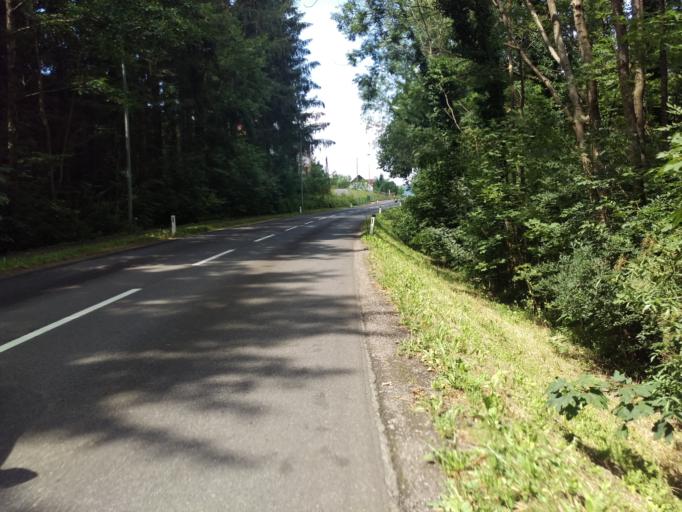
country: AT
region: Styria
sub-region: Politischer Bezirk Graz-Umgebung
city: Kumberg
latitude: 47.1373
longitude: 15.5221
